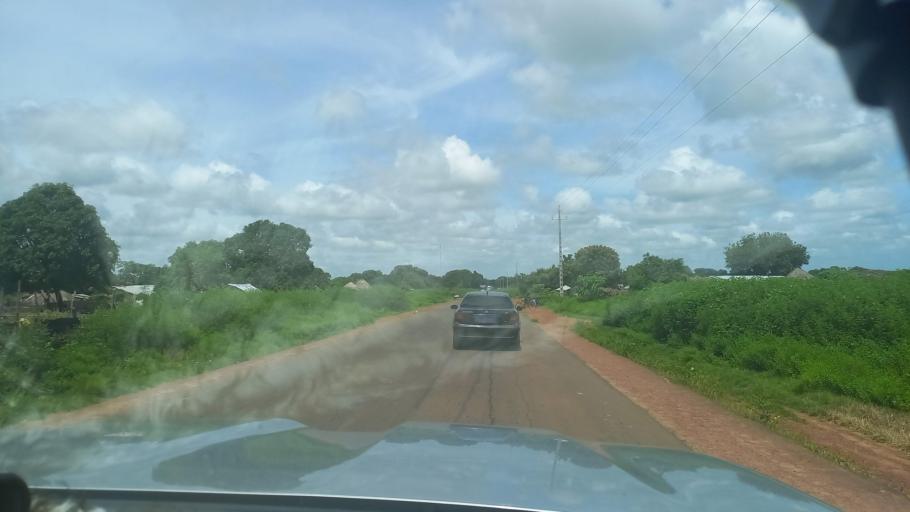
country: GM
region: Lower River
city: Kaiaf
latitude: 13.1987
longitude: -15.5523
